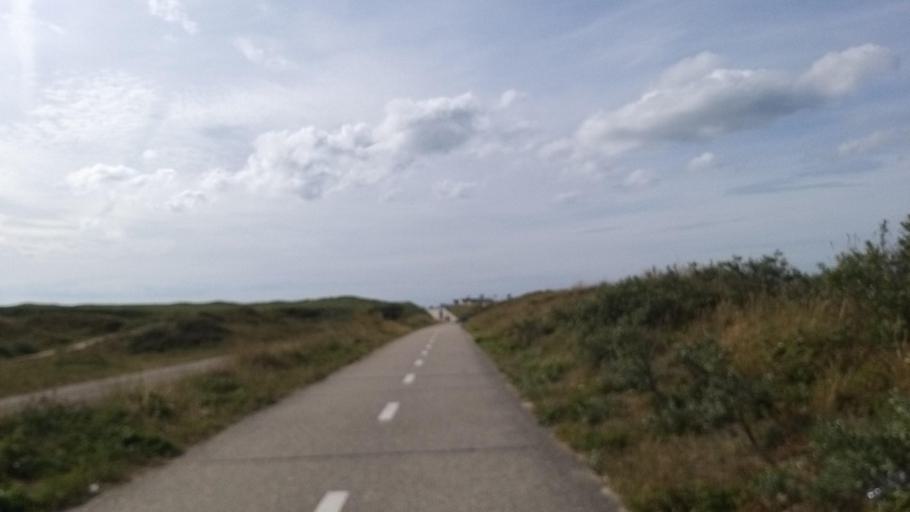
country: NL
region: North Holland
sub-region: Gemeente Texel
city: Den Burg
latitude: 53.1602
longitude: 4.8256
